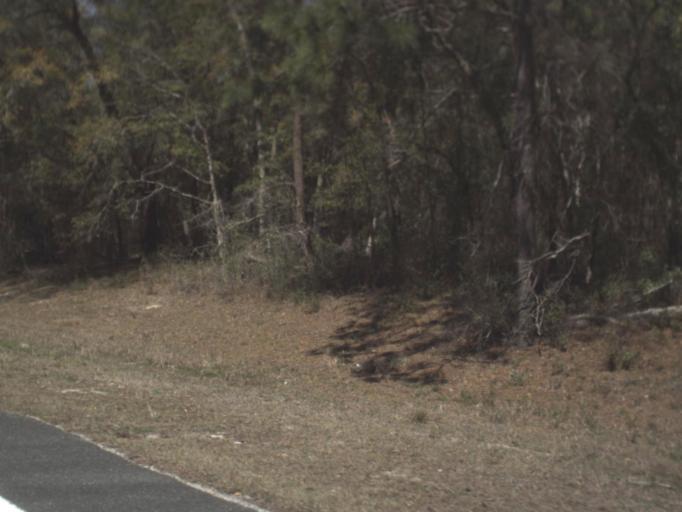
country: US
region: Florida
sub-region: Wakulla County
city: Crawfordville
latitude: 30.2877
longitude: -84.4014
